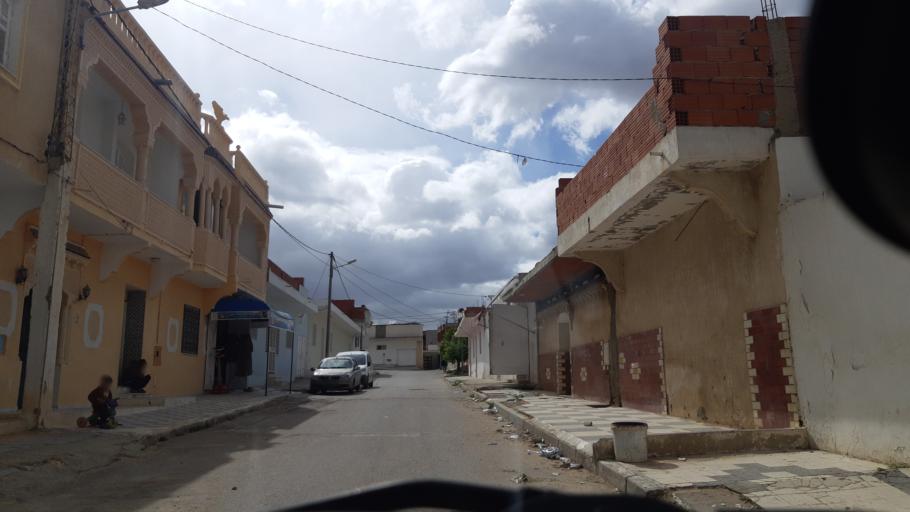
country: TN
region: Susah
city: Akouda
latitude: 35.8692
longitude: 10.5236
